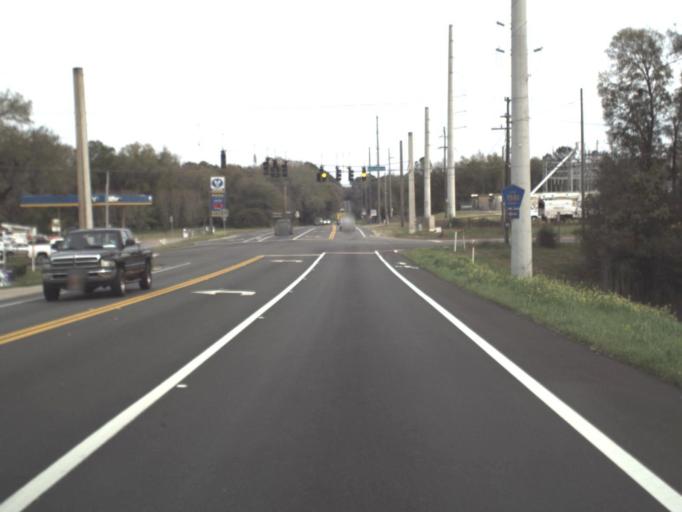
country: US
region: Florida
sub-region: Leon County
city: Tallahassee
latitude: 30.4359
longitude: -84.3749
